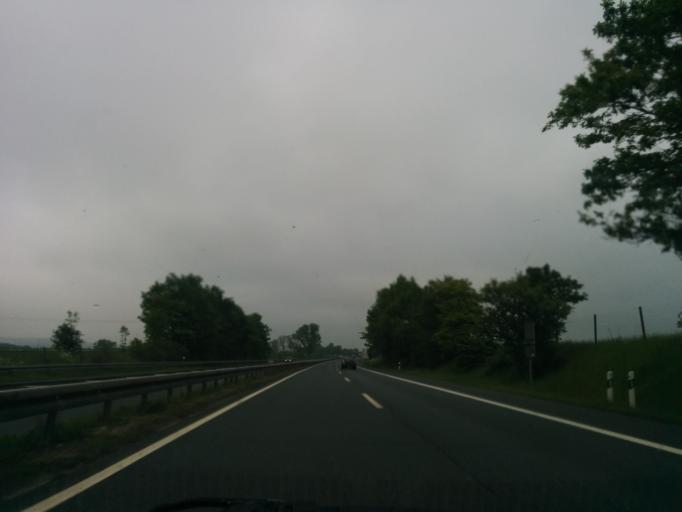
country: DE
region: Lower Saxony
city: Vienenburg
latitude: 51.9239
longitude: 10.5586
